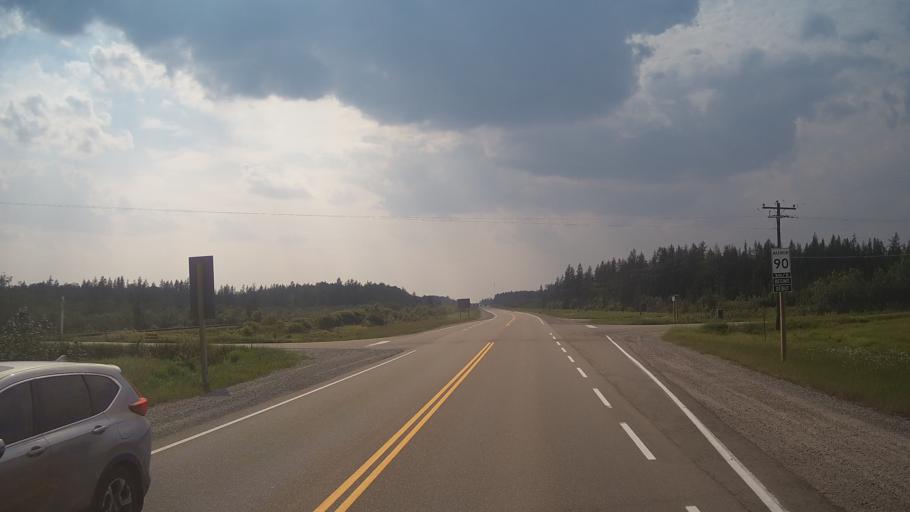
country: CA
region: Ontario
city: Kapuskasing
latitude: 49.5287
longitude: -82.8770
